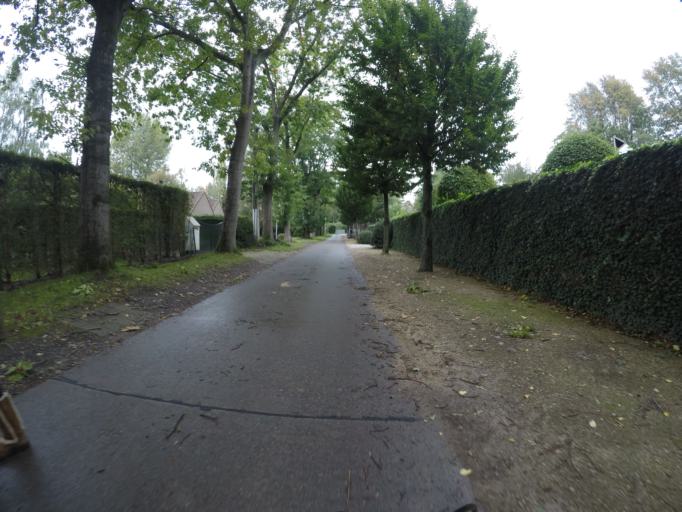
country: BE
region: Flanders
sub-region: Provincie West-Vlaanderen
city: Oostkamp
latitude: 51.1713
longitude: 3.1873
